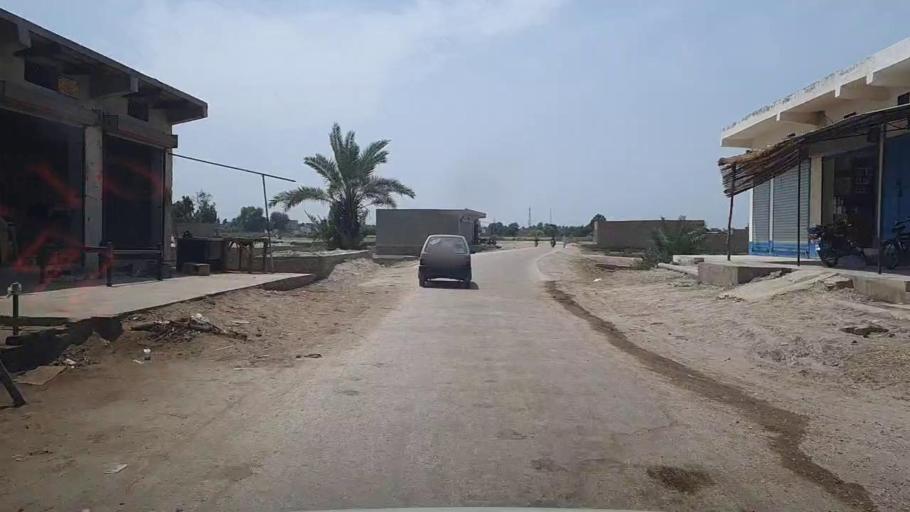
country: PK
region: Sindh
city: Pano Aqil
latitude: 27.8560
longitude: 69.1230
